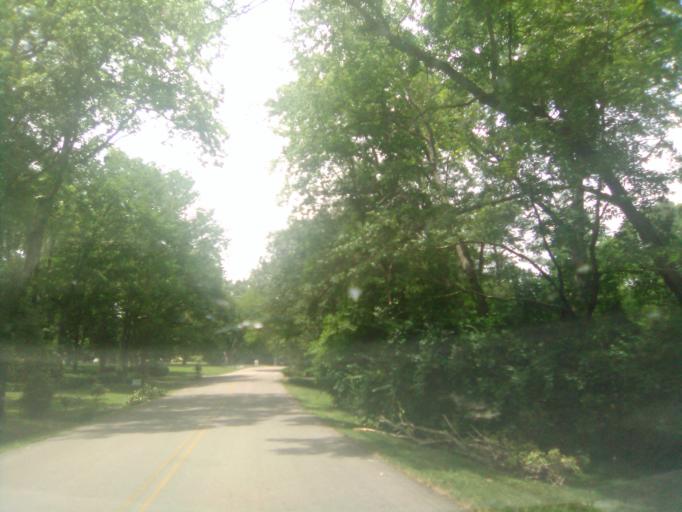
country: US
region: Tennessee
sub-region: Davidson County
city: Forest Hills
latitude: 36.0817
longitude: -86.8512
